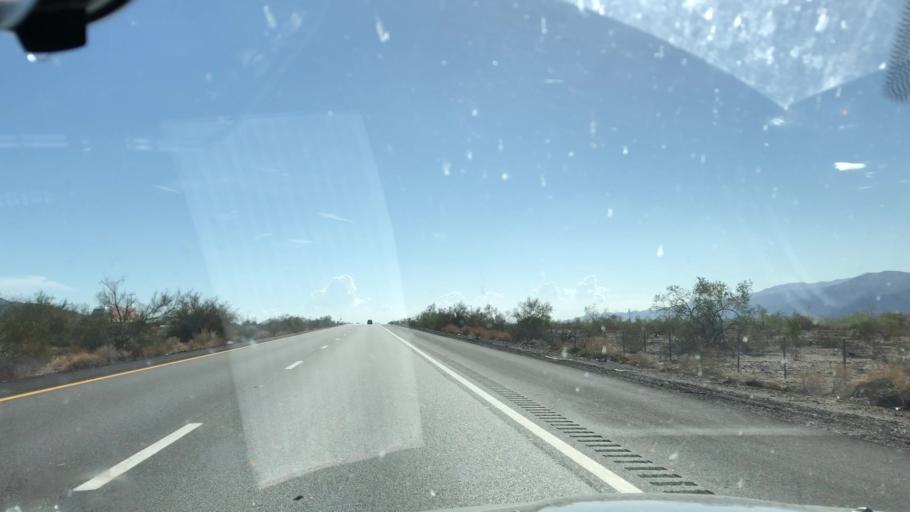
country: US
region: California
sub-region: Imperial County
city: Niland
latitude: 33.6892
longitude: -115.5129
